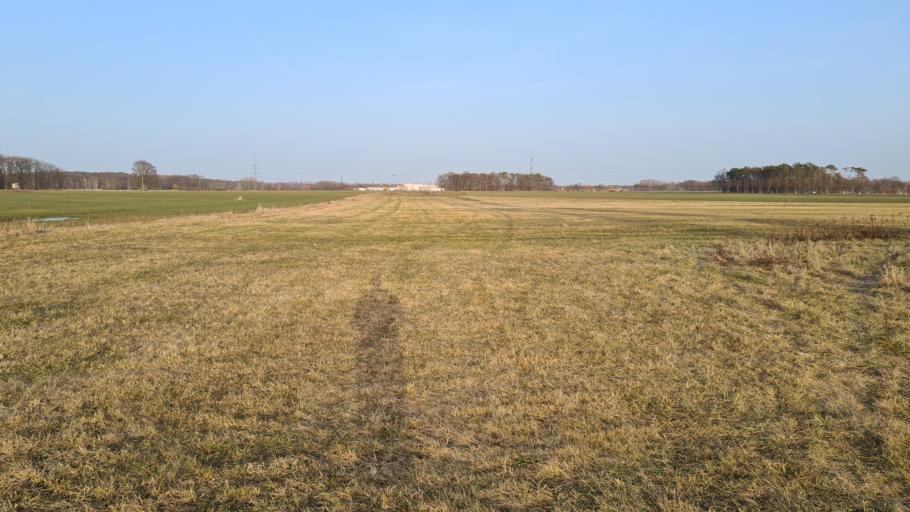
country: DE
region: Brandenburg
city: Schonborn
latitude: 51.6007
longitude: 13.5163
